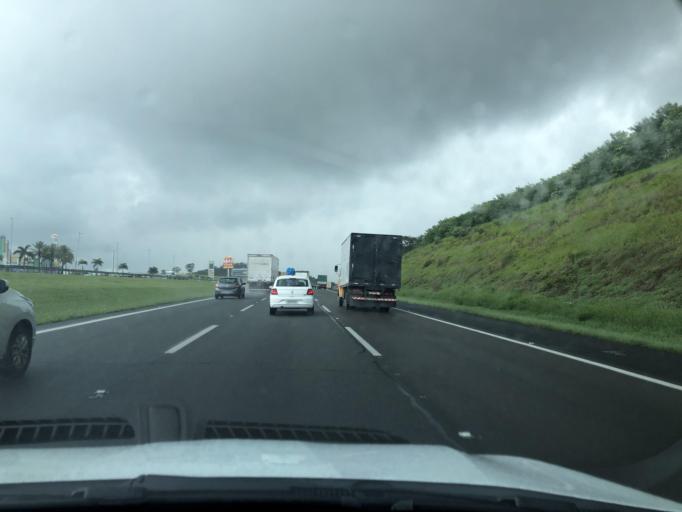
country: BR
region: Sao Paulo
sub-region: Jundiai
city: Jundiai
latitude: -23.2058
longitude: -46.9253
